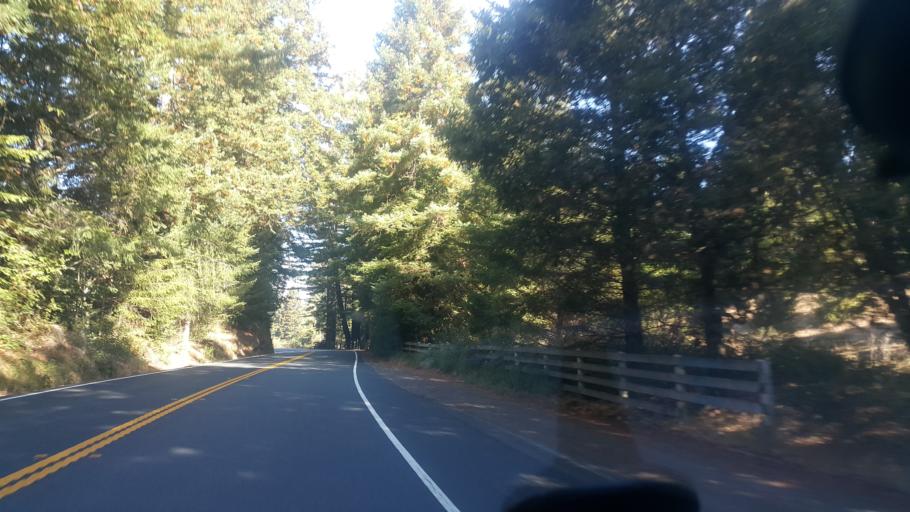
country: US
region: California
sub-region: Mendocino County
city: Fort Bragg
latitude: 39.3523
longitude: -123.6081
